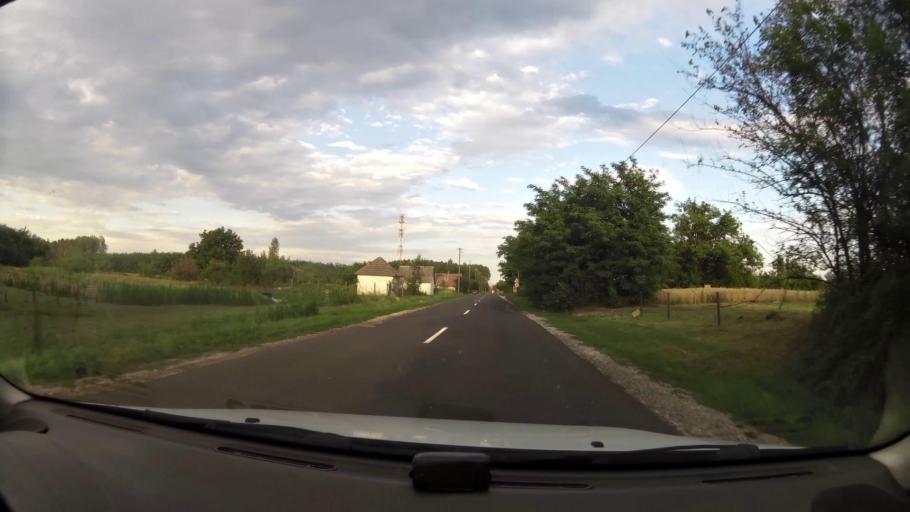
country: HU
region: Pest
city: Tapioszentmarton
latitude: 47.3465
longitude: 19.7211
